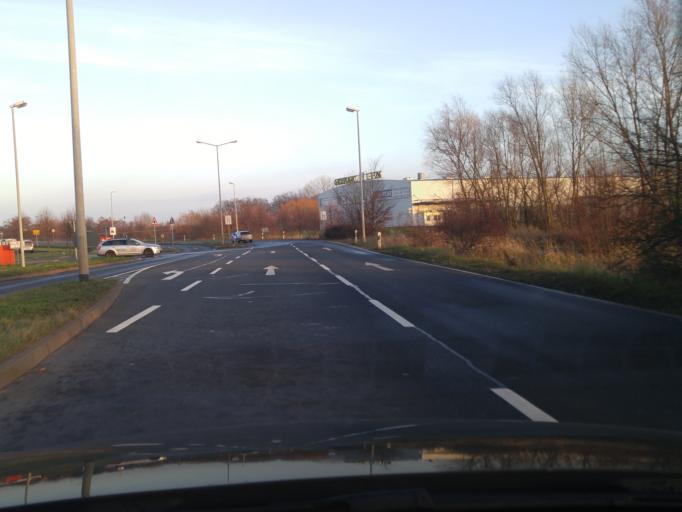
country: DE
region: Saxony
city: Zwochau
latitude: 51.4130
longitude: 12.3074
